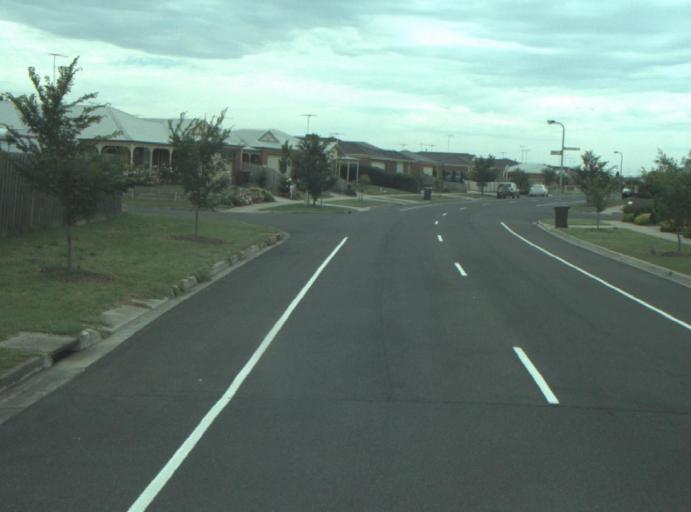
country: AU
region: Victoria
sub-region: Greater Geelong
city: Breakwater
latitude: -38.1944
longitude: 144.3916
